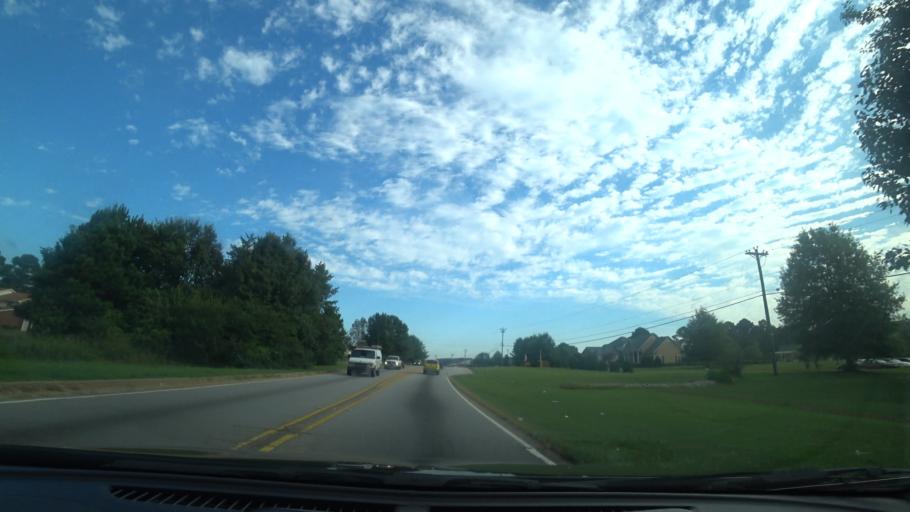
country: US
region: Georgia
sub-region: Rockdale County
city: Conyers
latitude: 33.6210
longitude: -83.9766
